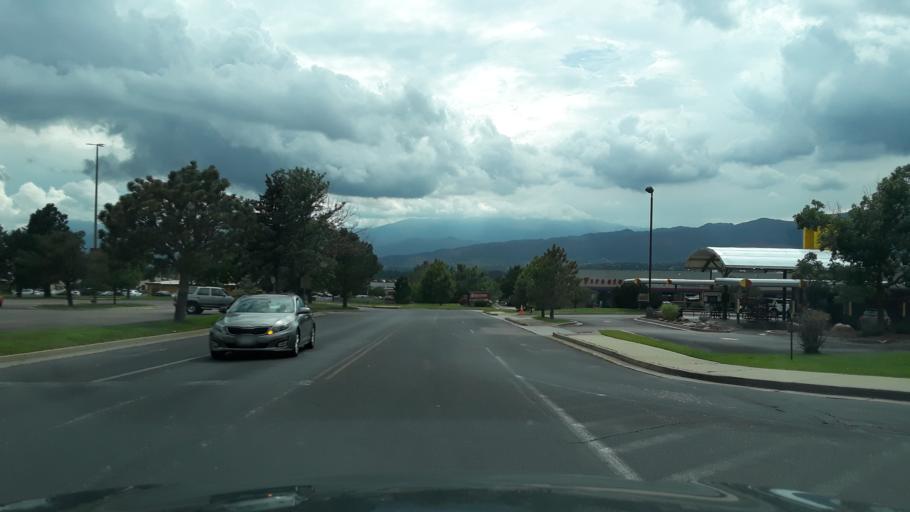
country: US
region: Colorado
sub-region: El Paso County
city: Air Force Academy
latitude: 38.9477
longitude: -104.7990
